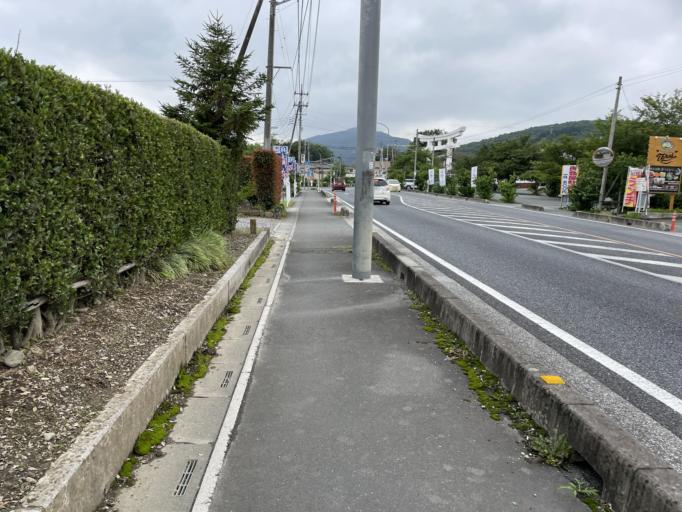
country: JP
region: Saitama
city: Yorii
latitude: 36.0953
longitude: 139.1105
